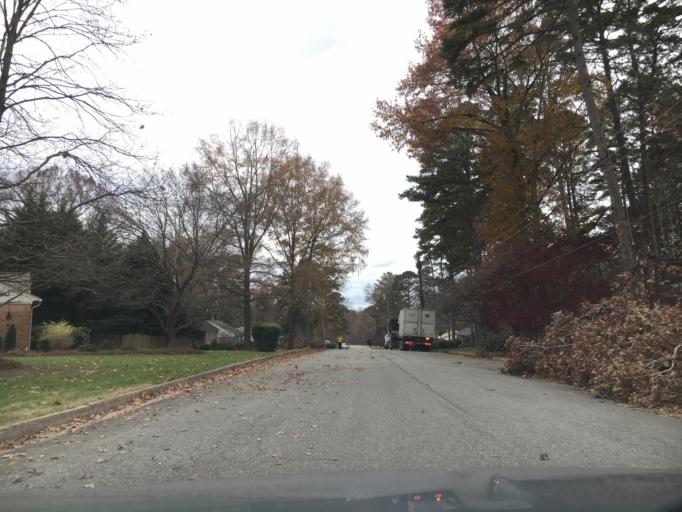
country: US
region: Virginia
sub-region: Halifax County
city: South Boston
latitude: 36.7289
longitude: -78.9078
